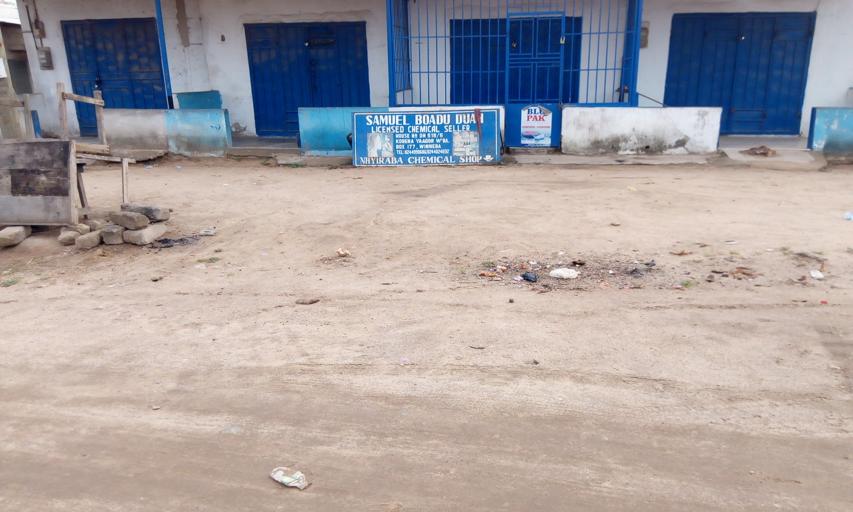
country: GH
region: Central
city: Winneba
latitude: 5.3569
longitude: -0.6187
